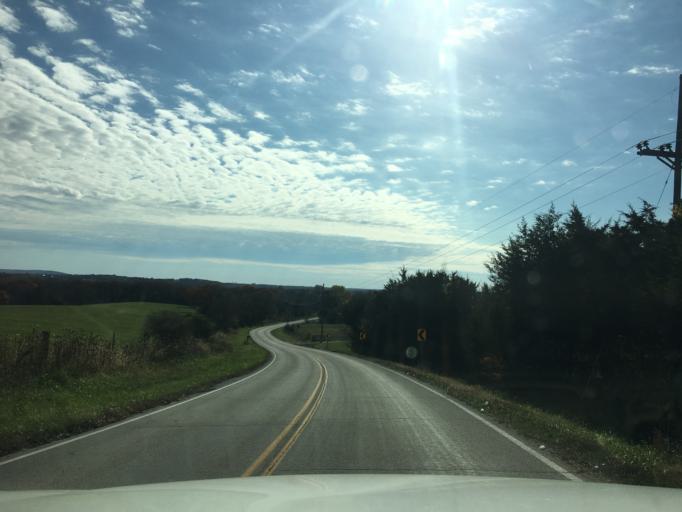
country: US
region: Missouri
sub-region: Osage County
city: Linn
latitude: 38.4087
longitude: -91.8170
